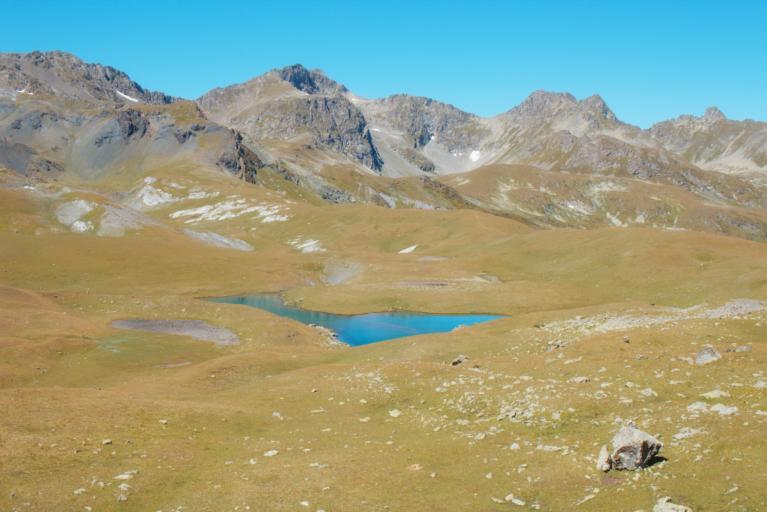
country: RU
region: Karachayevo-Cherkesiya
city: Nizhniy Arkhyz
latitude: 43.6038
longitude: 41.1652
